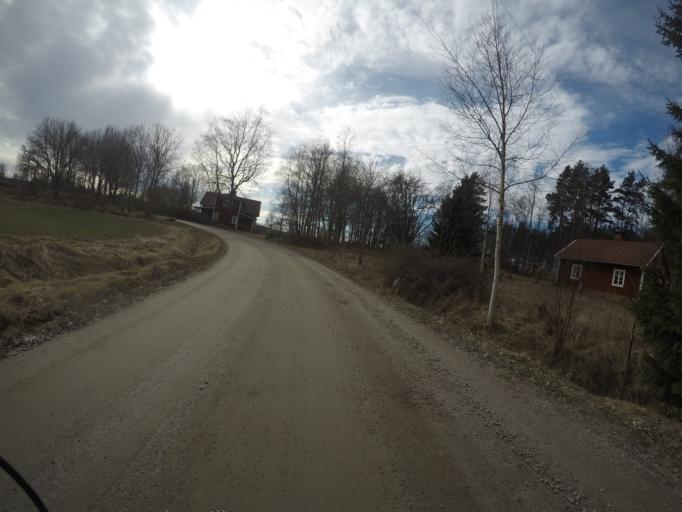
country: SE
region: Vaestmanland
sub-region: Kungsors Kommun
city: Kungsoer
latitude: 59.4203
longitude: 16.2106
